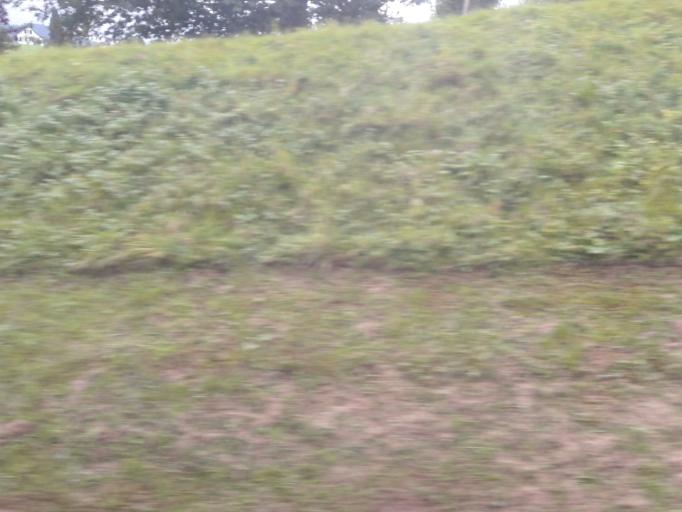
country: CH
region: Zurich
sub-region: Bezirk Horgen
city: Richterswil
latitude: 47.1956
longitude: 8.6872
